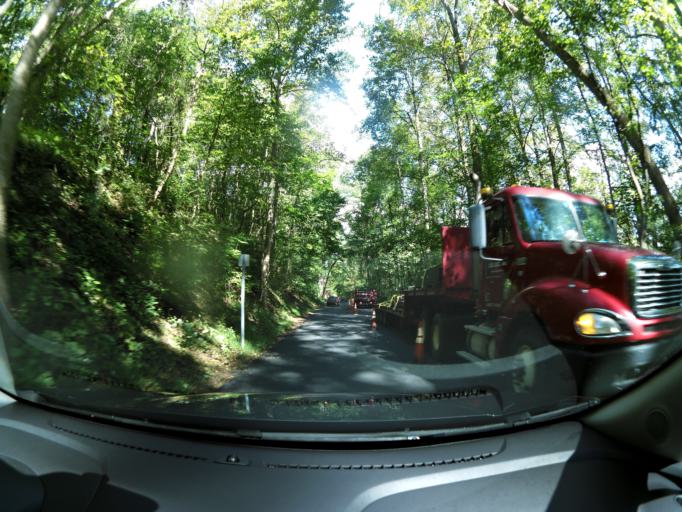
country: US
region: Virginia
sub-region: Fairfax County
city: Great Falls
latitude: 38.9934
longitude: -77.2557
